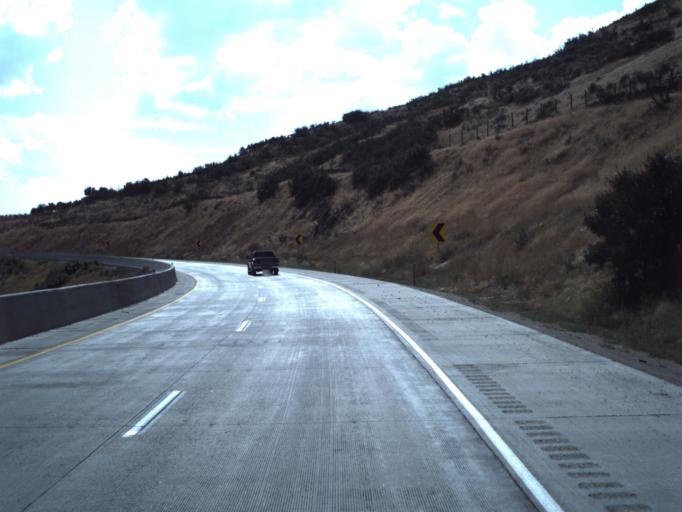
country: US
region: Utah
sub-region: Summit County
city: Snyderville
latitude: 40.7914
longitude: -111.4522
